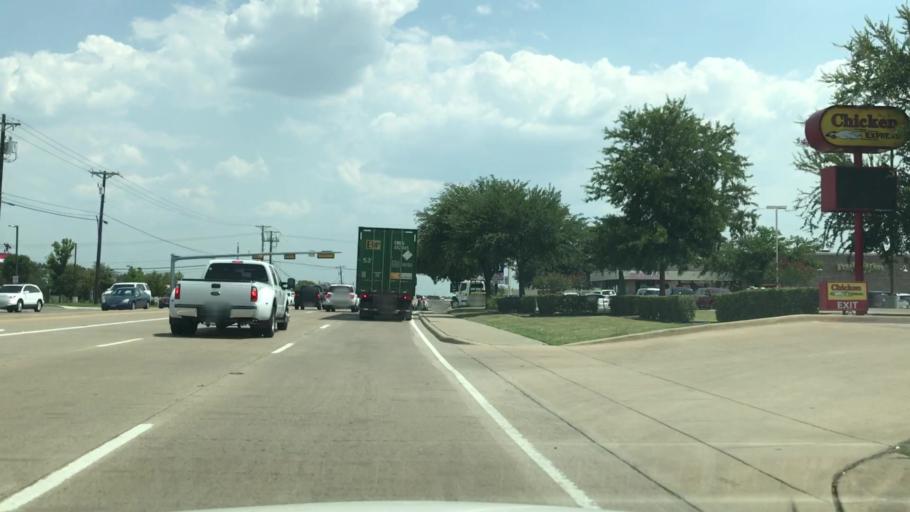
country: US
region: Texas
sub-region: Rockwall County
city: Rockwall
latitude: 32.9136
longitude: -96.4533
